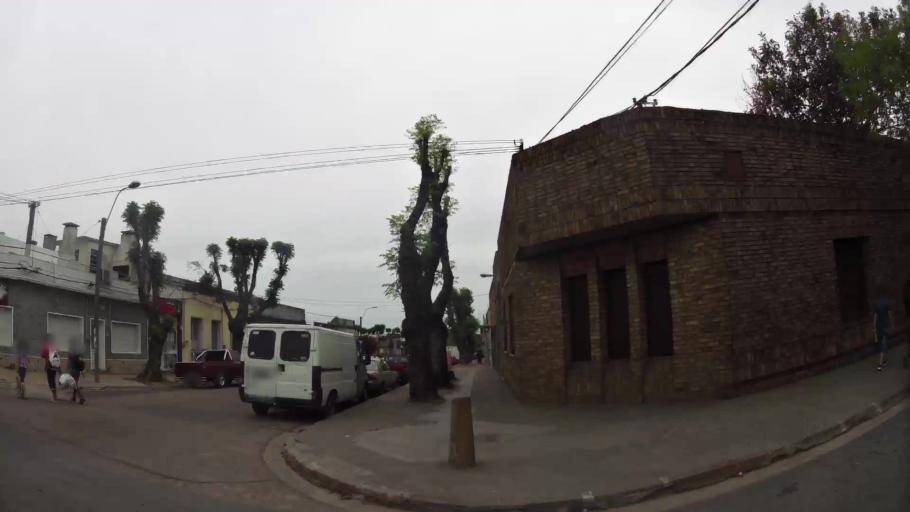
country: UY
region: Canelones
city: Las Piedras
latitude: -34.7269
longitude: -56.2125
